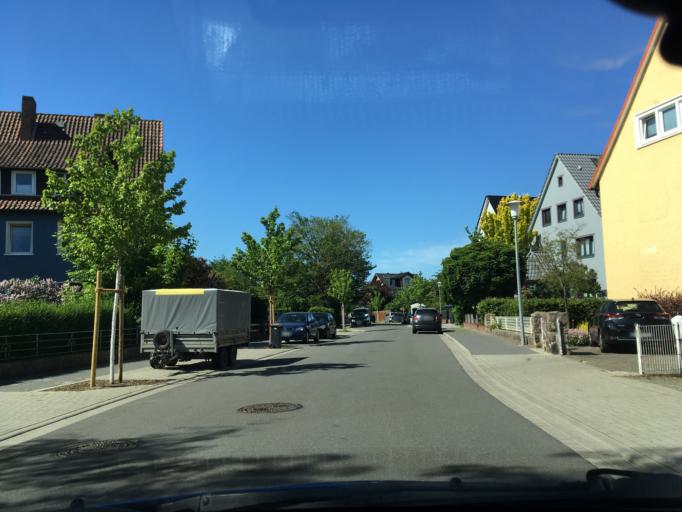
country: DE
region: Lower Saxony
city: Uelzen
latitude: 52.9598
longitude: 10.5523
